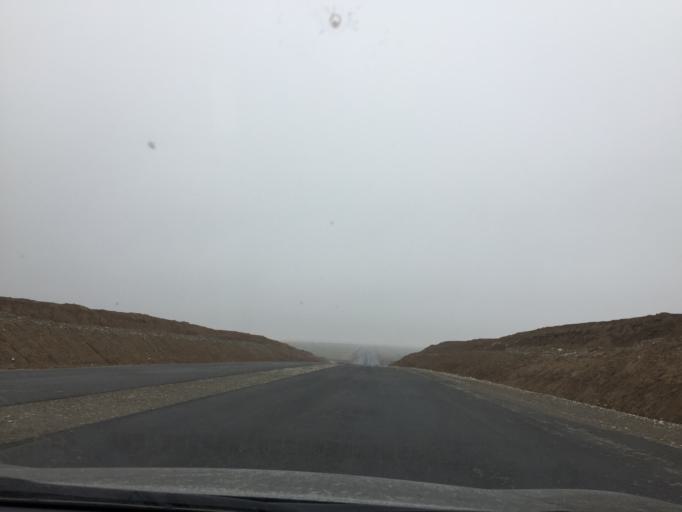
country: KZ
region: Ongtustik Qazaqstan
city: Turar Ryskulov
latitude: 42.5083
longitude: 70.4052
